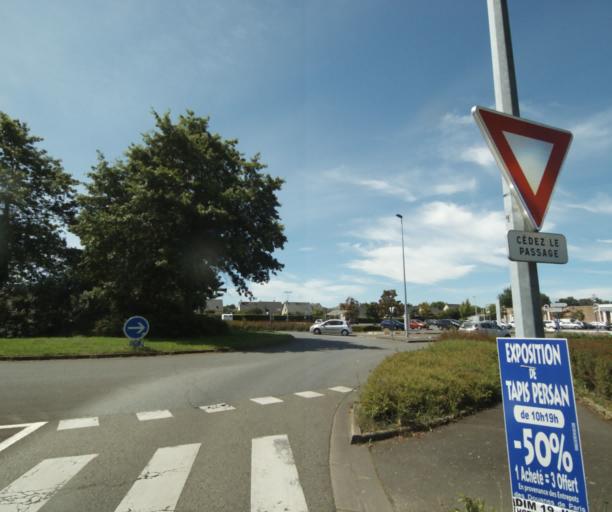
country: FR
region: Pays de la Loire
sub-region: Departement de la Mayenne
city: Change
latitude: 48.0786
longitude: -0.8016
